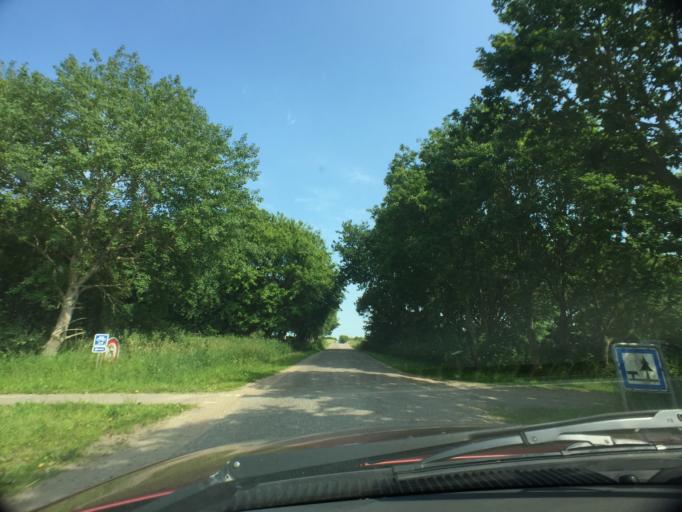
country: DK
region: Central Jutland
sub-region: Viborg Kommune
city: Bjerringbro
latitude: 56.2524
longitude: 9.7198
